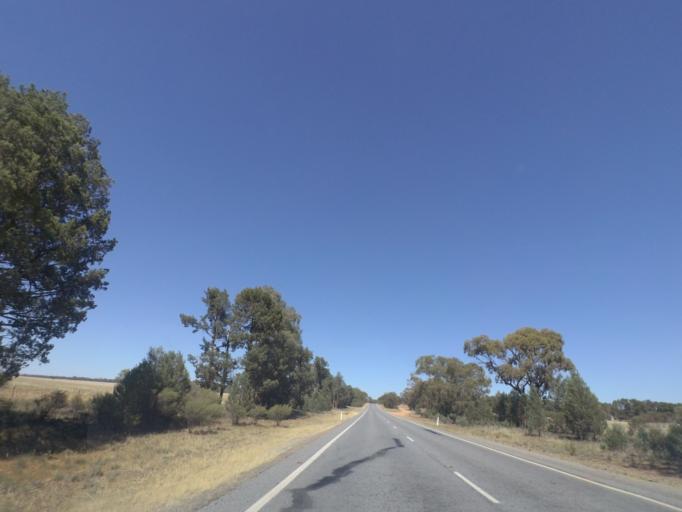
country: AU
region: New South Wales
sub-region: Narrandera
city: Narrandera
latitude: -34.4169
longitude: 146.8559
